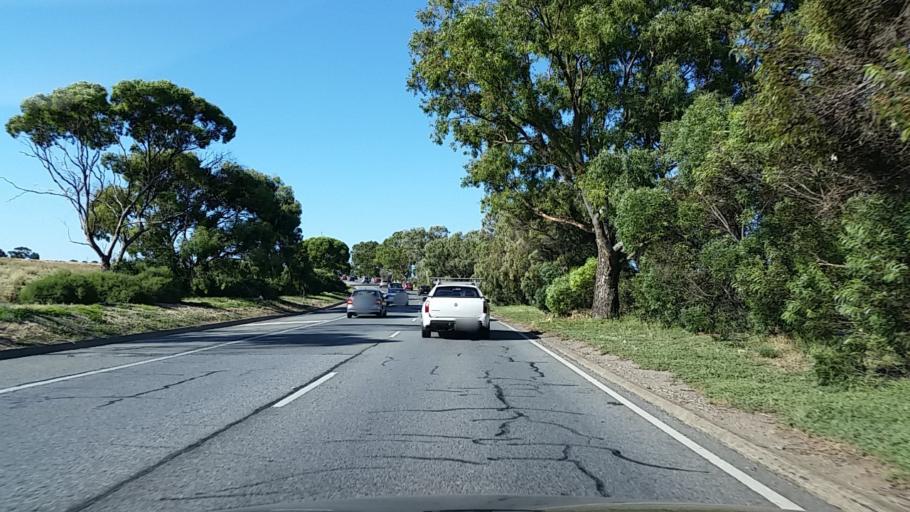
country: AU
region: South Australia
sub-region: Marion
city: Trott Park
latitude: -35.0640
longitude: 138.5337
